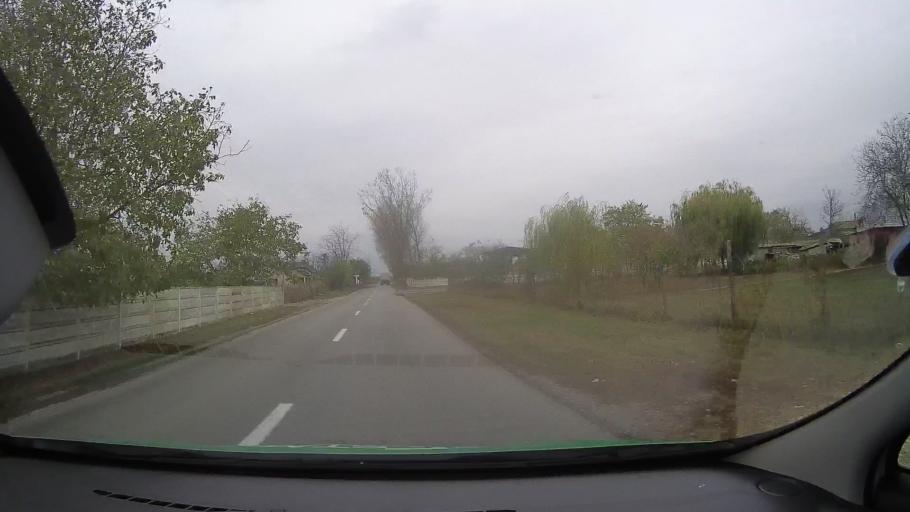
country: RO
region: Constanta
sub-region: Comuna Mihail Kogalniceanu
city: Mihail Kogalniceanu
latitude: 44.3800
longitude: 28.4641
